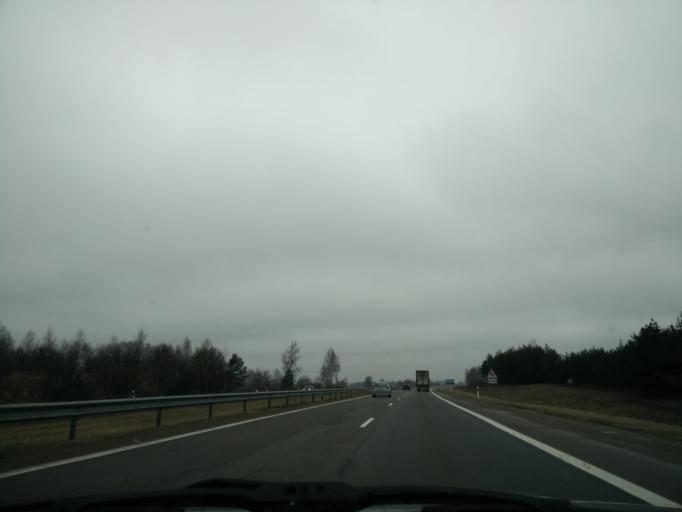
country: LT
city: Skaudvile
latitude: 55.4198
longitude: 22.7776
